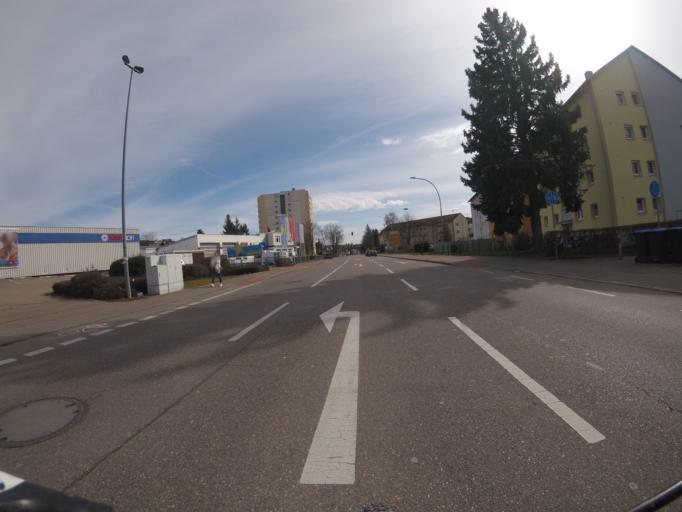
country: DE
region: Baden-Wuerttemberg
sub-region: Regierungsbezirk Stuttgart
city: Backnang
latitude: 48.9591
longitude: 9.4304
